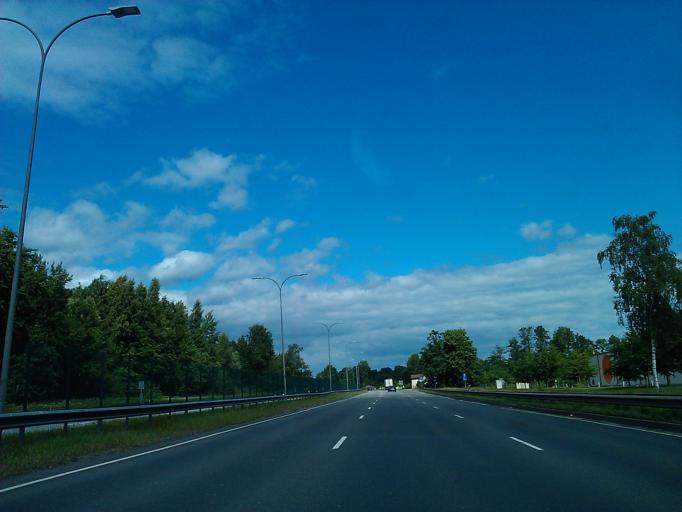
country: LV
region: Marupe
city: Marupe
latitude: 56.9430
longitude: 23.9967
